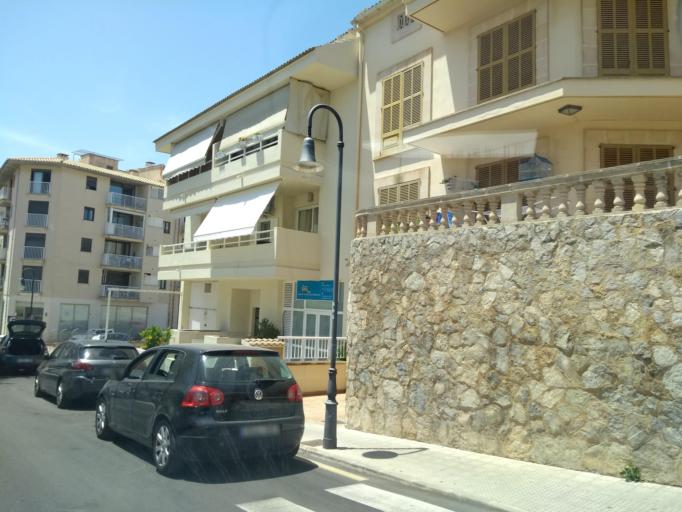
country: ES
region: Balearic Islands
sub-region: Illes Balears
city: Port d'Alcudia
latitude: 39.8418
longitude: 3.1378
